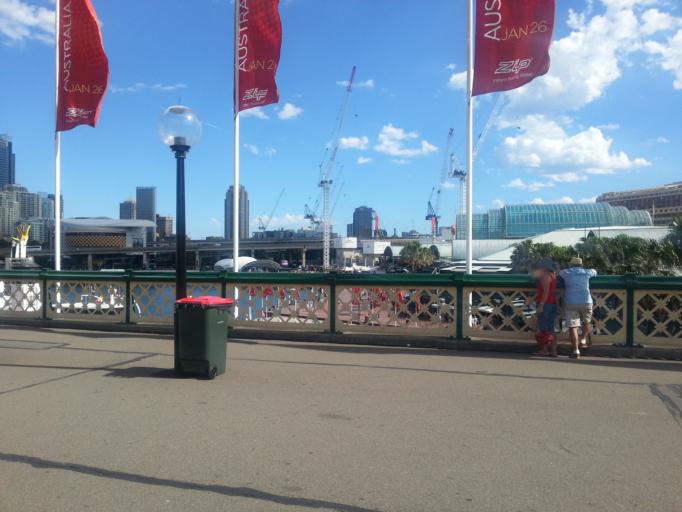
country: AU
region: New South Wales
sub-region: City of Sydney
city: Sydney
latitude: -33.8703
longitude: 151.1992
